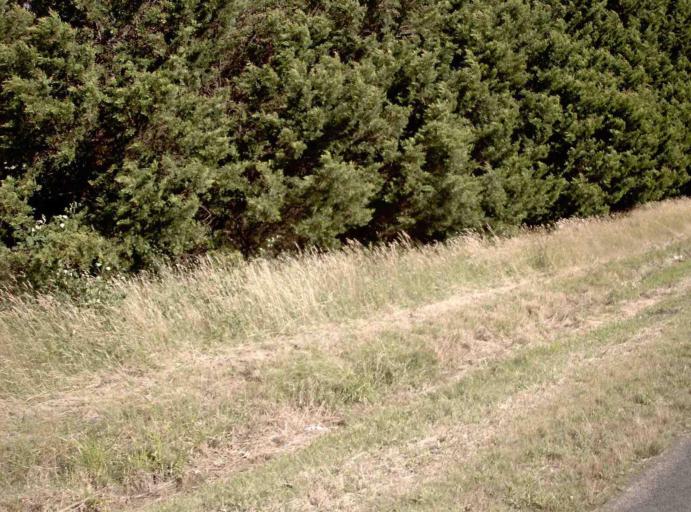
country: AU
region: Victoria
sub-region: Latrobe
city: Morwell
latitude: -38.2961
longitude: 146.4231
